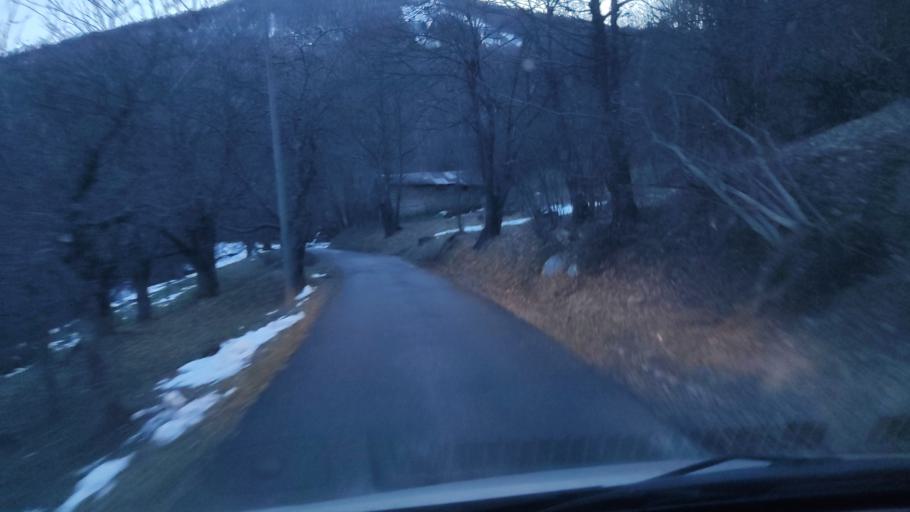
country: IT
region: Piedmont
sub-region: Provincia di Cuneo
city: Viola
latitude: 44.2792
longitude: 7.9637
